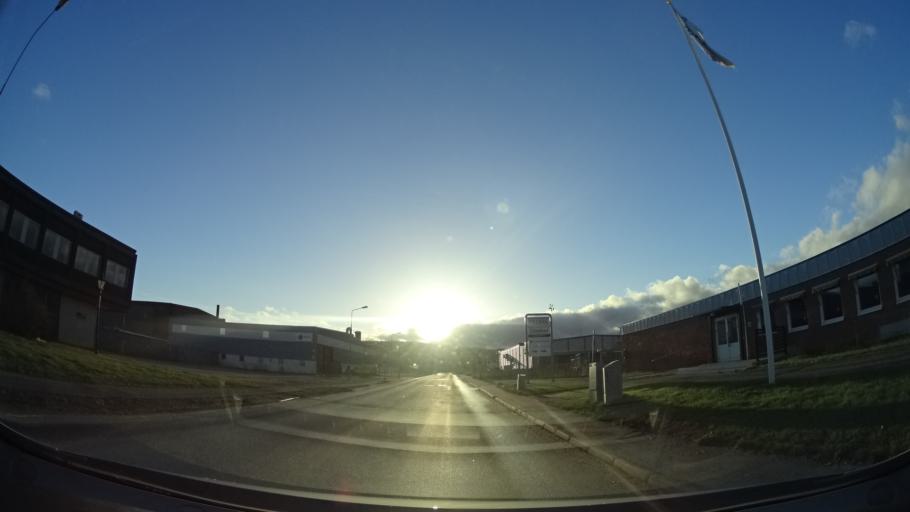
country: SE
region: Vaesterbotten
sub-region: Skelleftea Kommun
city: Soedra Bergsbyn
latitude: 64.7446
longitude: 21.0303
